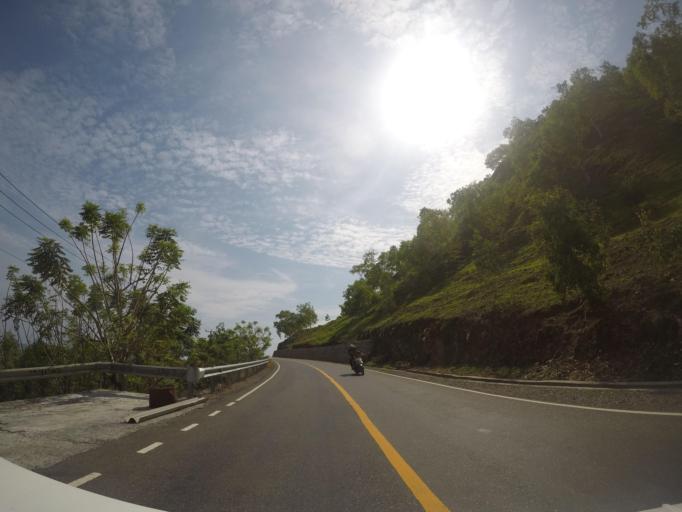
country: TL
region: Manatuto
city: Manatuto
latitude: -8.4794
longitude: 125.9102
